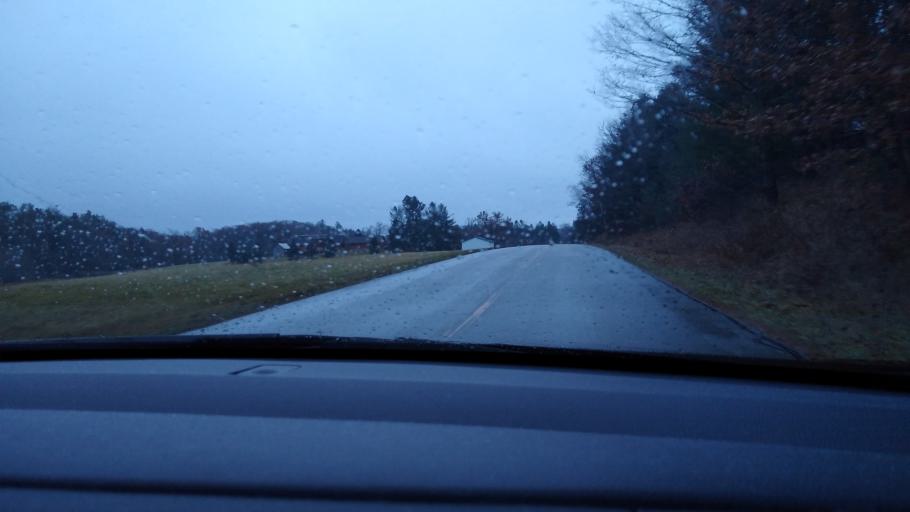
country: US
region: Michigan
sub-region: Wexford County
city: Cadillac
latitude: 44.1897
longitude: -85.3955
